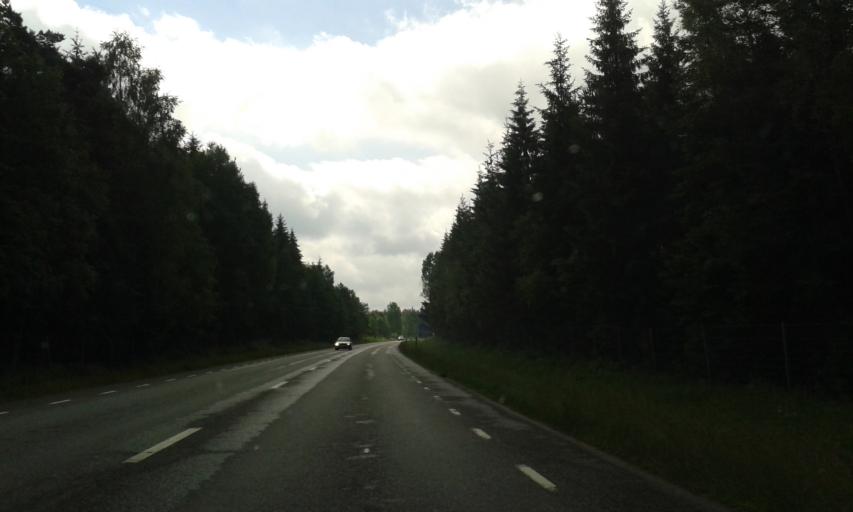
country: SE
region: Vaestra Goetaland
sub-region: Tranemo Kommun
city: Limmared
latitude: 57.5406
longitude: 13.3352
